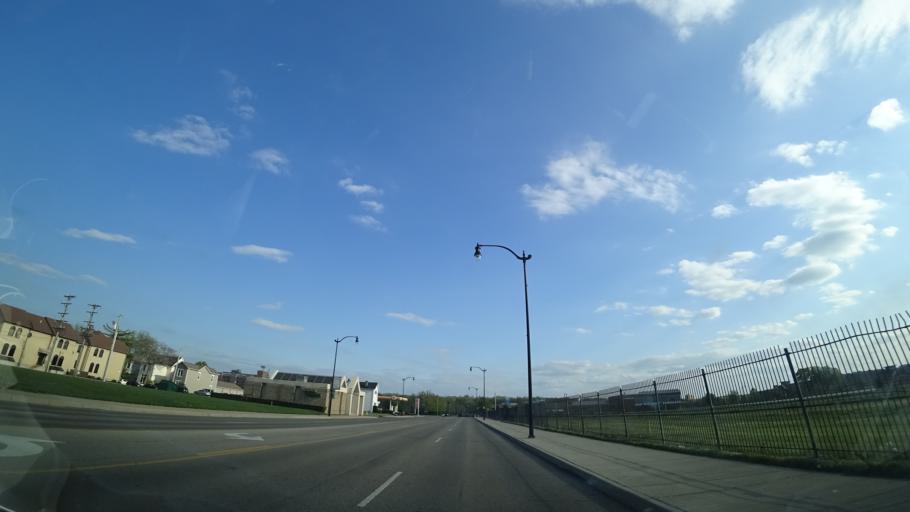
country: US
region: Ohio
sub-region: Montgomery County
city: Dayton
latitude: 39.7419
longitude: -84.1871
